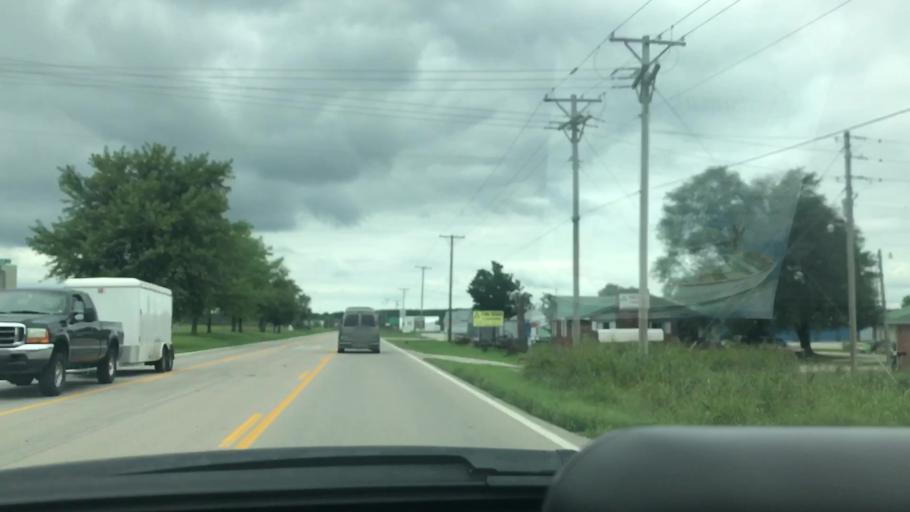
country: US
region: Missouri
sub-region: Dallas County
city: Buffalo
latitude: 37.6547
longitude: -93.1037
